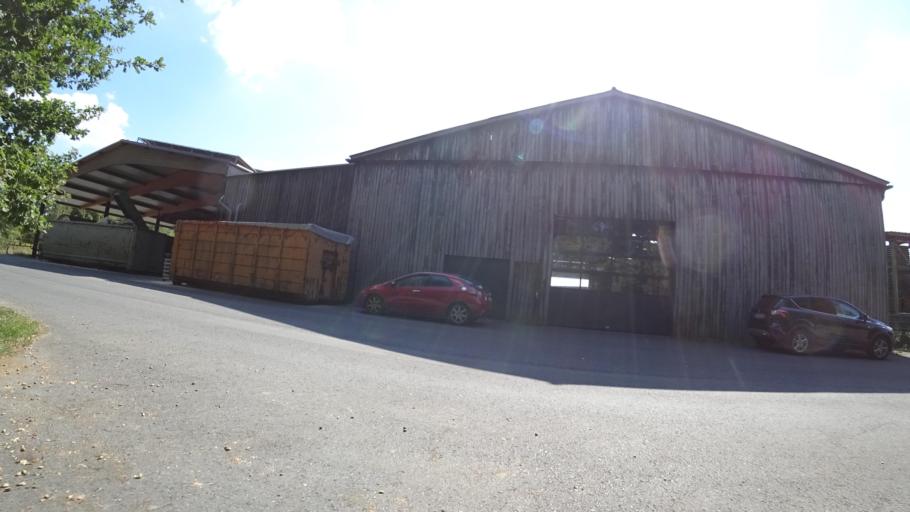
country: DE
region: North Rhine-Westphalia
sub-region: Regierungsbezirk Detmold
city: Rheda-Wiedenbruck
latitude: 51.8882
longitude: 8.2795
